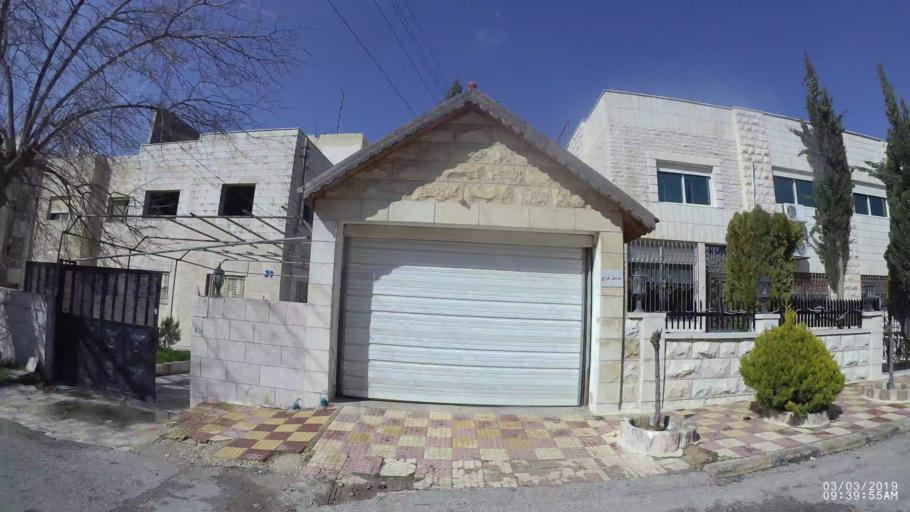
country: JO
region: Amman
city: Al Jubayhah
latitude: 31.9992
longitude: 35.8985
